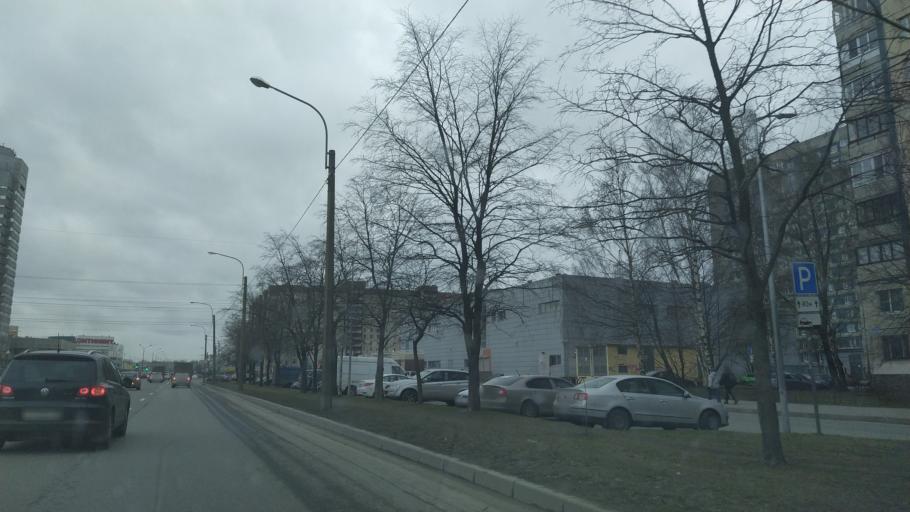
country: RU
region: St.-Petersburg
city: Komendantsky aerodrom
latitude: 60.0083
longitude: 30.2737
